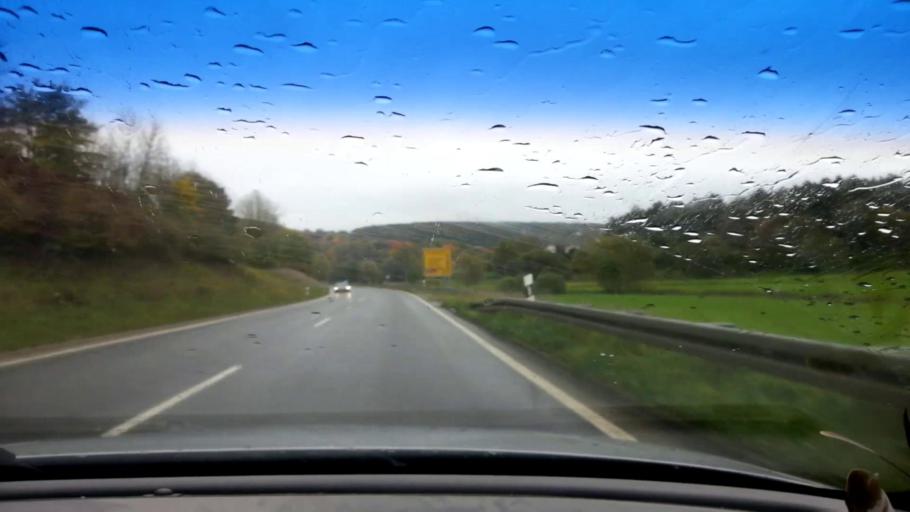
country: DE
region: Bavaria
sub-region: Upper Franconia
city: Heiligenstadt
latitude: 49.8677
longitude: 11.1611
